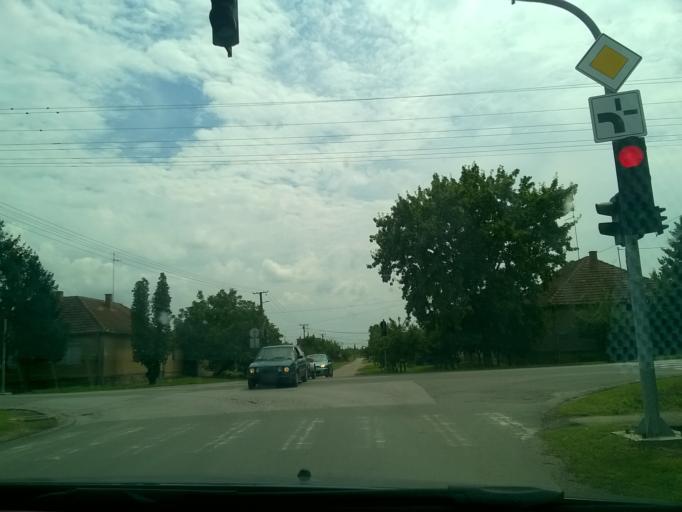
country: RS
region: Autonomna Pokrajina Vojvodina
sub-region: Juznobanatski Okrug
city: Plandiste
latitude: 45.2266
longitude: 21.1214
